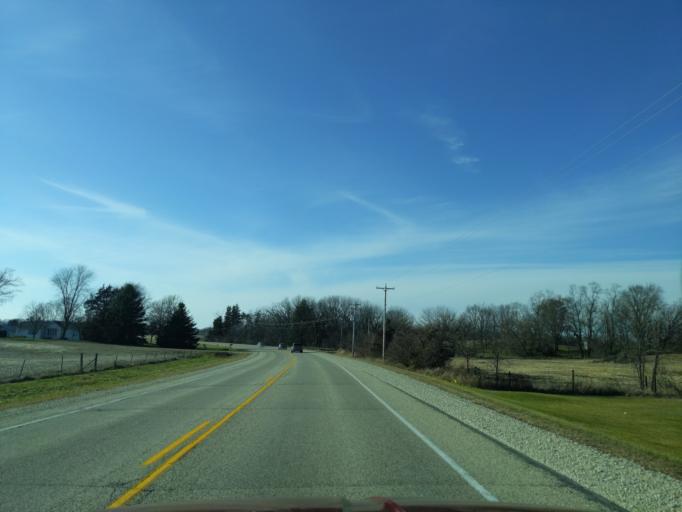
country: US
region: Wisconsin
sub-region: Rock County
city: Milton
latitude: 42.8300
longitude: -88.8698
